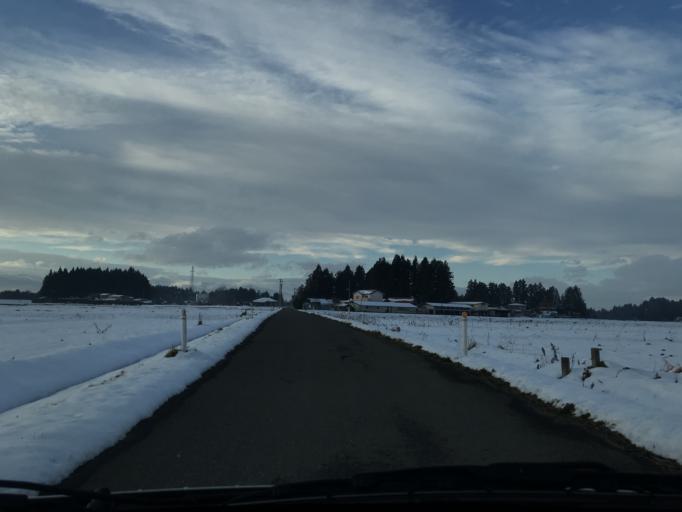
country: JP
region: Iwate
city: Mizusawa
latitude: 39.0609
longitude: 141.0881
